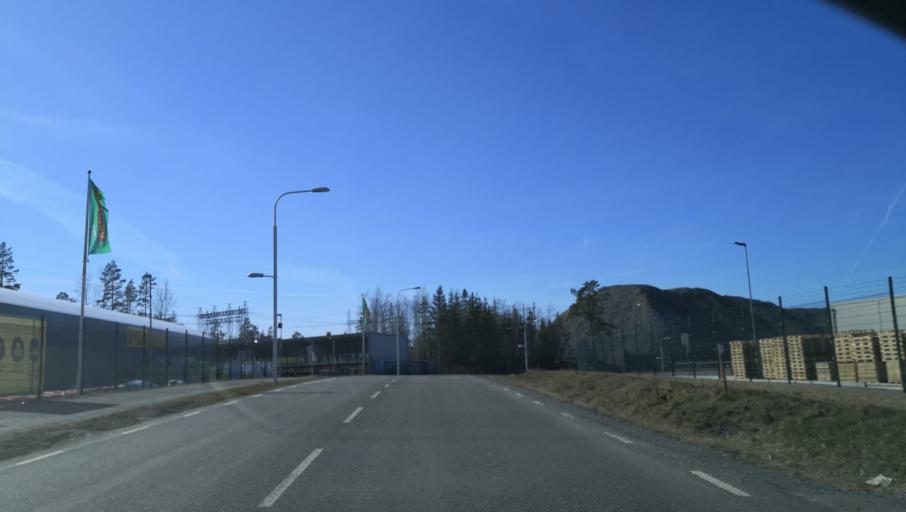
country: SE
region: Stockholm
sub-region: Varmdo Kommun
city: Gustavsberg
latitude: 59.3118
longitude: 18.3735
